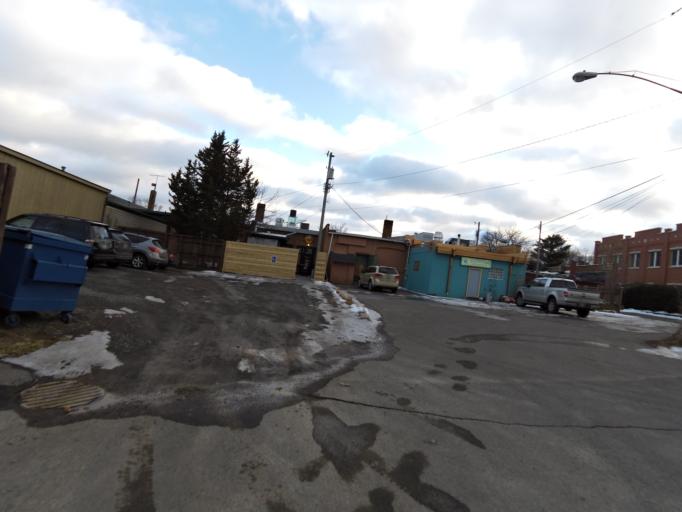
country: US
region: Minnesota
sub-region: Washington County
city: Bayport
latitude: 45.0221
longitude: -92.7816
